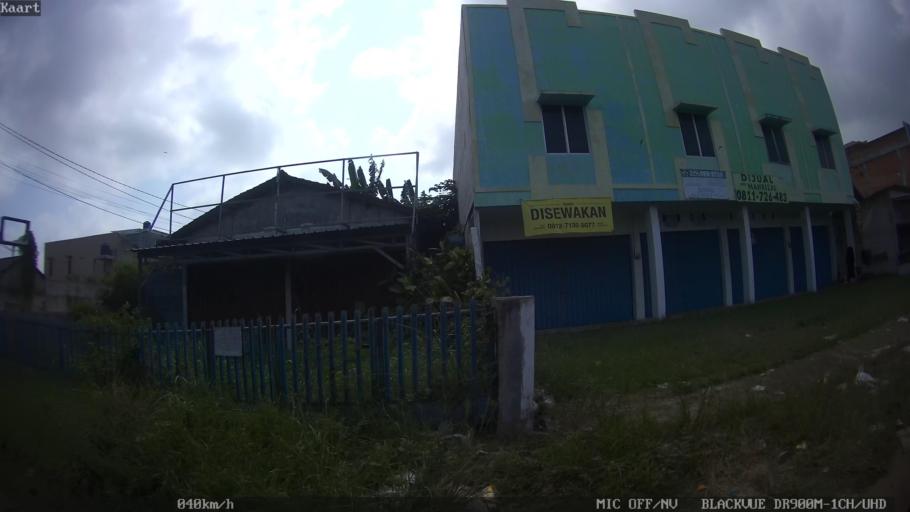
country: ID
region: Lampung
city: Kedaton
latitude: -5.3280
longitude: 105.2902
